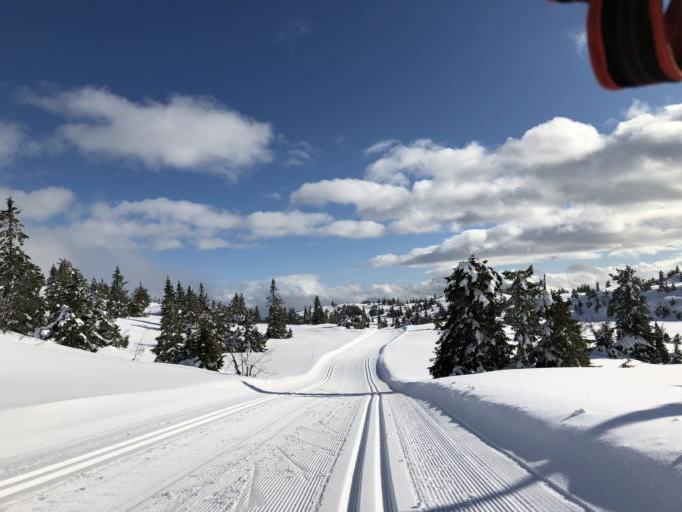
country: NO
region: Oppland
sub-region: Gausdal
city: Segalstad bru
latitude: 61.3320
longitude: 10.0307
